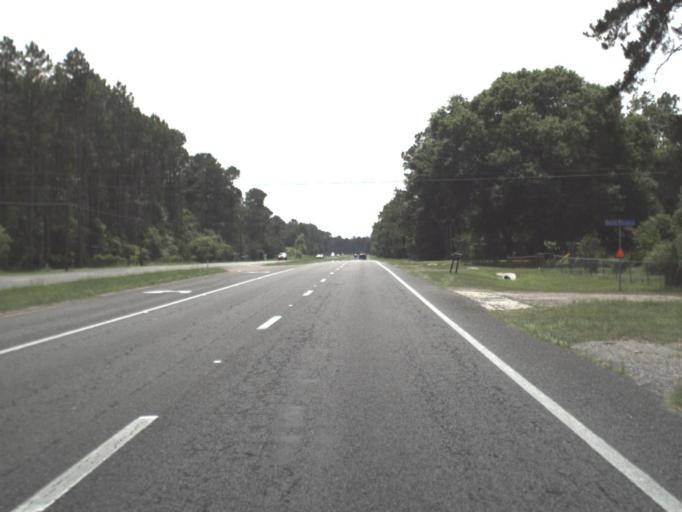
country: US
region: Florida
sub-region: Nassau County
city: Nassau Village-Ratliff
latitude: 30.5235
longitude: -81.8010
